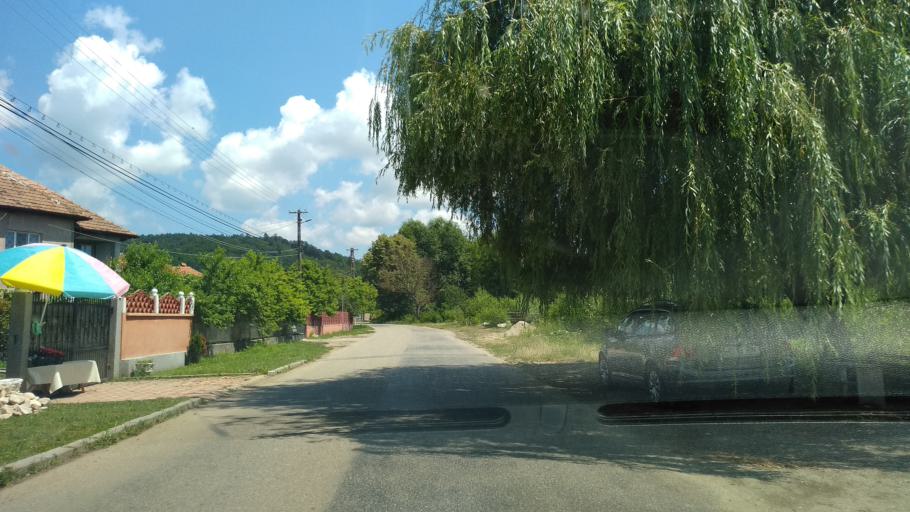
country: RO
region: Hunedoara
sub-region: Comuna Bosorod
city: Bosorod
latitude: 45.7039
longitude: 23.0691
